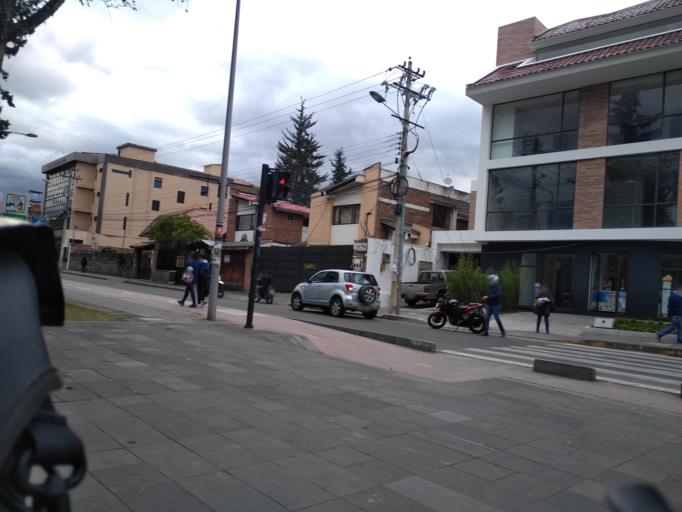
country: EC
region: Azuay
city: Cuenca
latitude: -2.9035
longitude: -79.0035
